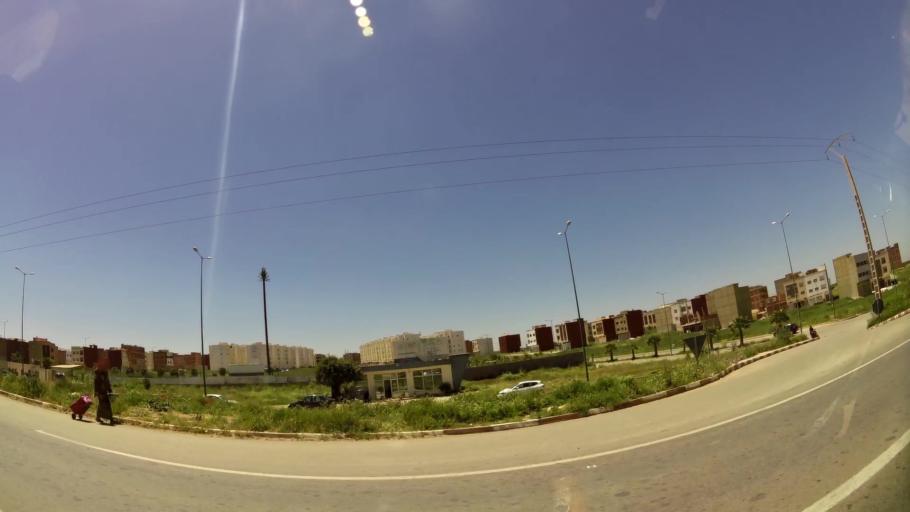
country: MA
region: Meknes-Tafilalet
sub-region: Meknes
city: Meknes
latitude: 33.8497
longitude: -5.5593
